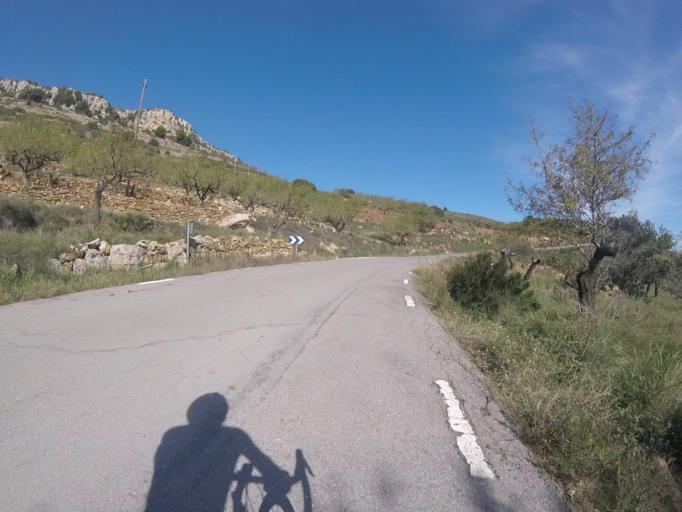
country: ES
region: Valencia
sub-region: Provincia de Castello
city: Sarratella
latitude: 40.2895
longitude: 0.0329
